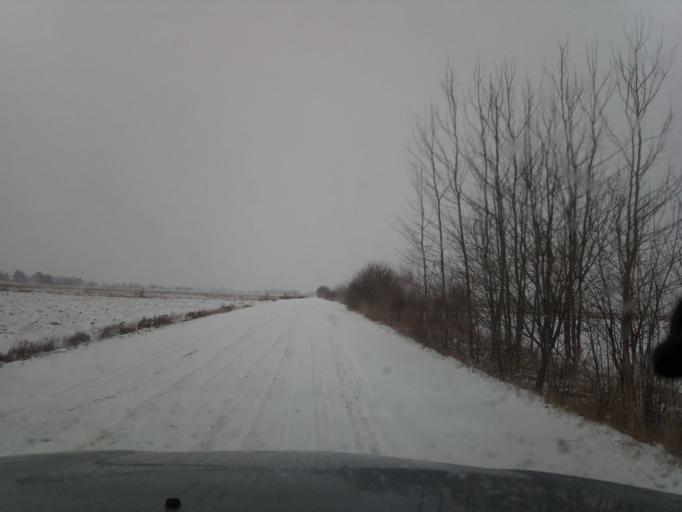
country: LT
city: Ramygala
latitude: 55.5590
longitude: 24.3708
